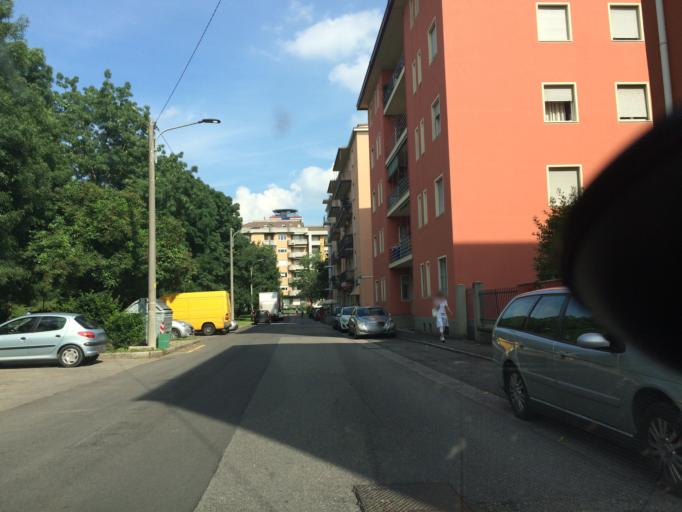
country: IT
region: Lombardy
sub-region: Provincia di Brescia
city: Brescia
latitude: 45.5265
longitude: 10.2073
